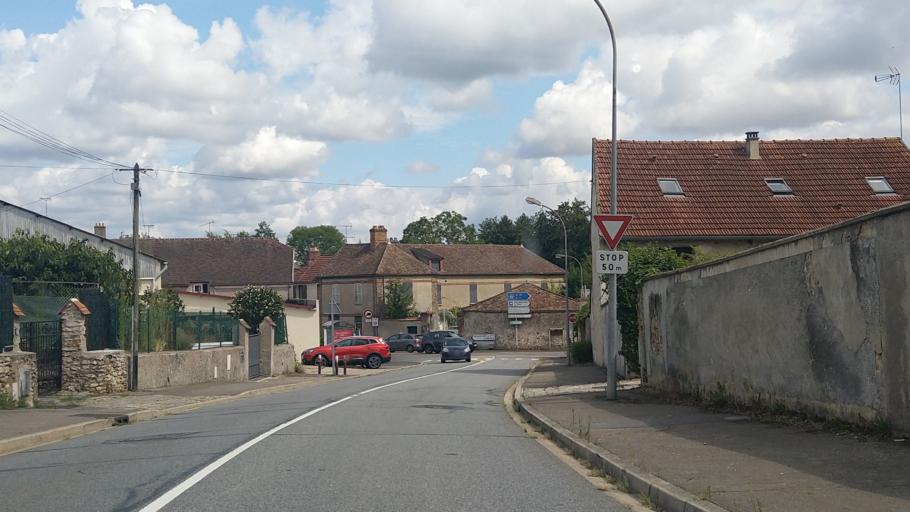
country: FR
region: Ile-de-France
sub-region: Departement des Yvelines
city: Saint-Arnoult-en-Yvelines
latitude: 48.5698
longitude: 1.9322
